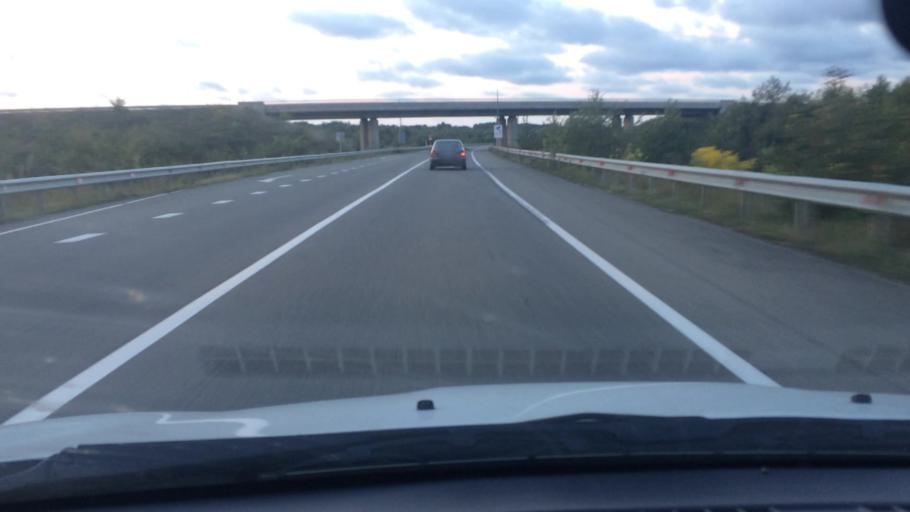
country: GE
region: Guria
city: Urek'i
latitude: 41.9167
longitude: 41.7768
